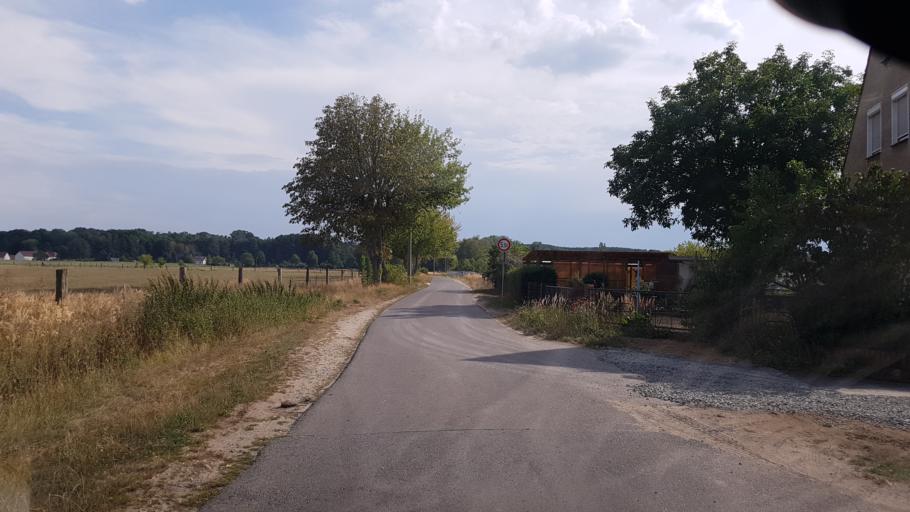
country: DE
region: Brandenburg
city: Hirschfeld
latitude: 51.3900
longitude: 13.6259
